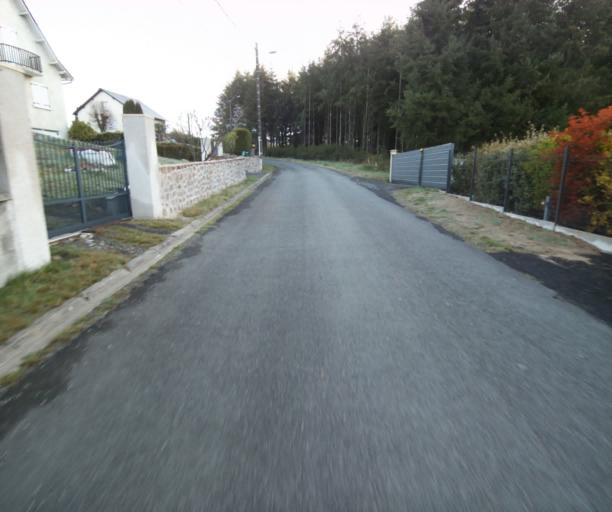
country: FR
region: Limousin
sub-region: Departement de la Correze
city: Correze
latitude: 45.3159
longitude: 1.8444
